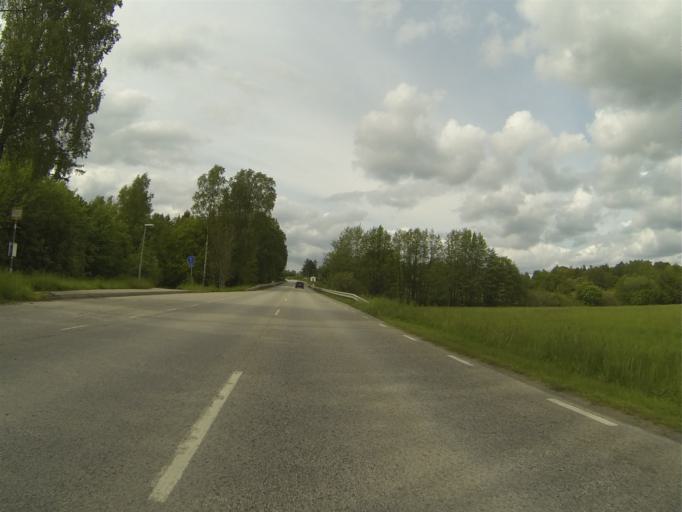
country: SE
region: Skane
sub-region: Lunds Kommun
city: Genarp
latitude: 55.6917
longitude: 13.3513
